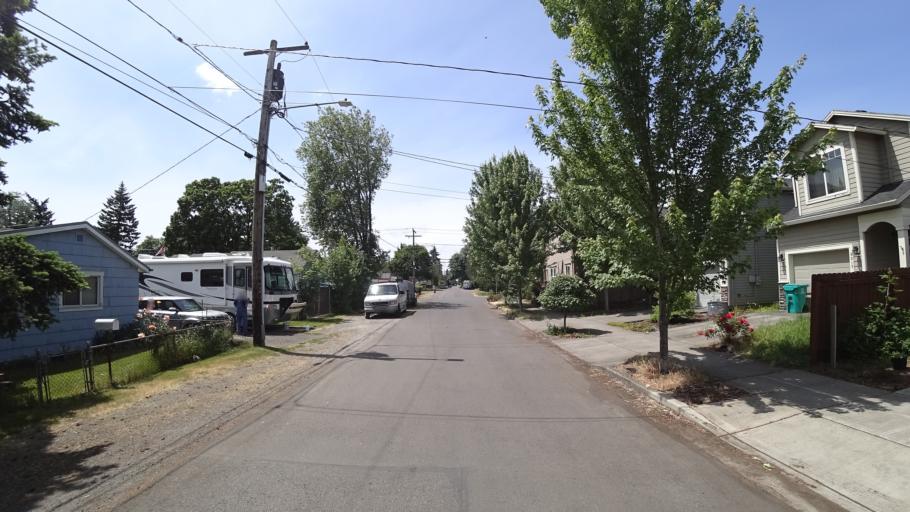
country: US
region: Oregon
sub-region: Multnomah County
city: Lents
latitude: 45.4673
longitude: -122.6016
